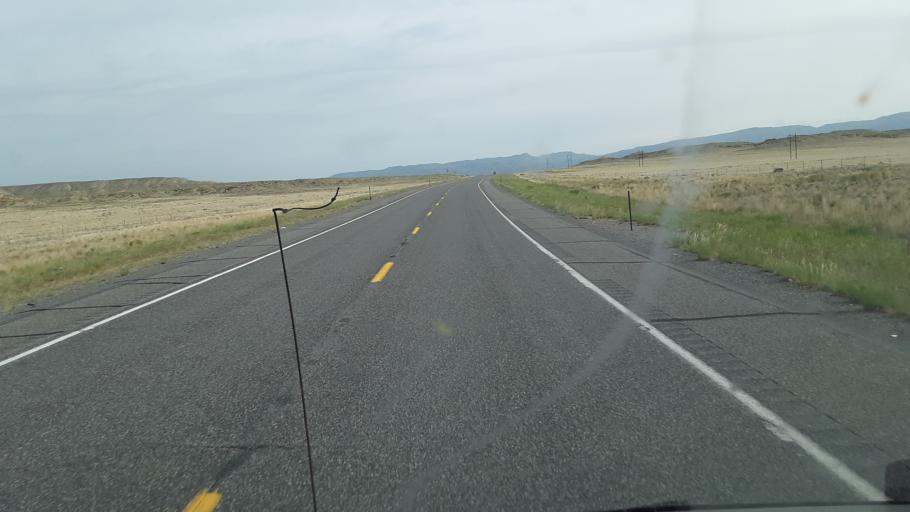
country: US
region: Wyoming
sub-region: Hot Springs County
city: Thermopolis
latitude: 43.2992
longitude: -108.1287
